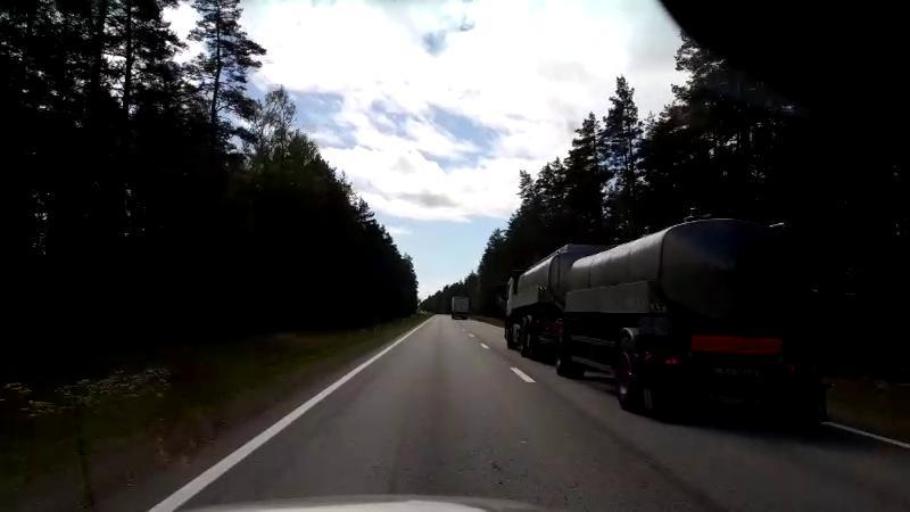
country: LV
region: Salacgrivas
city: Salacgriva
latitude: 57.5295
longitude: 24.4308
